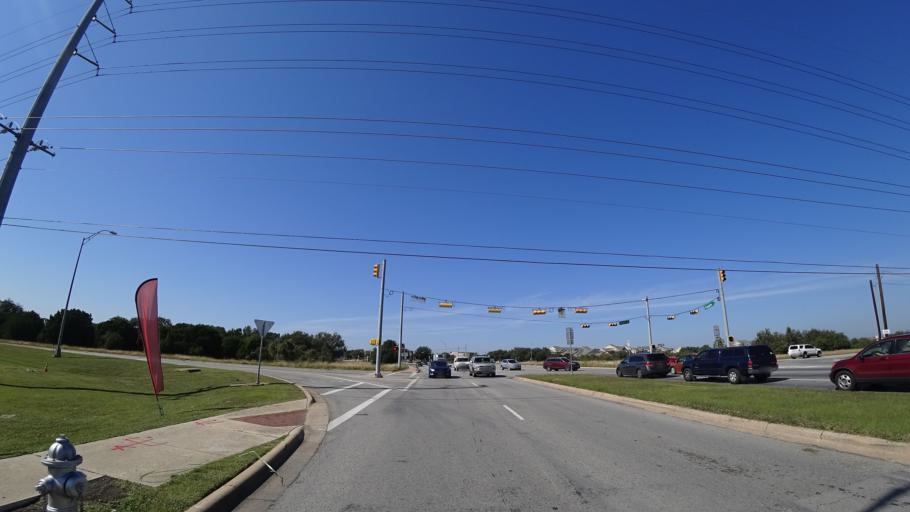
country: US
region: Texas
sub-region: Travis County
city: Shady Hollow
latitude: 30.2004
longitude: -97.8653
